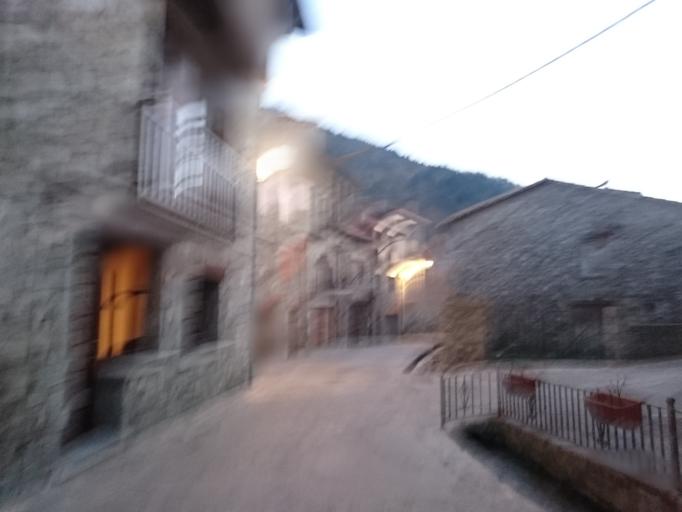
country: ES
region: Catalonia
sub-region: Provincia de Girona
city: Camprodon
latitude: 42.3759
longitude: 2.3018
